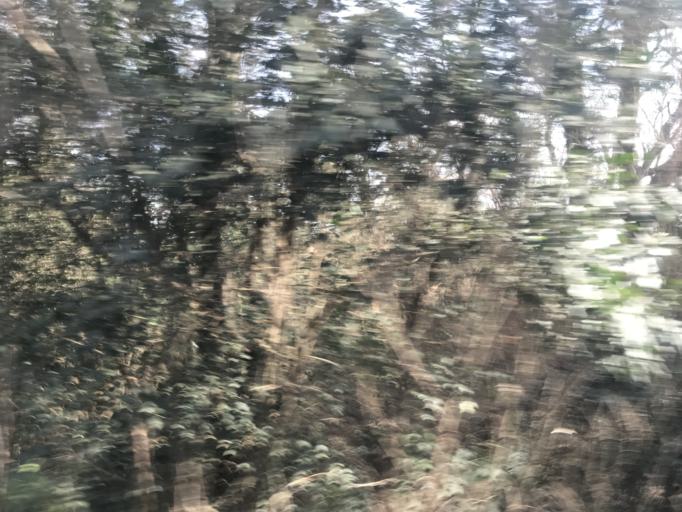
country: AR
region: Cordoba
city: Laguna Larga
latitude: -31.8093
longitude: -63.7745
